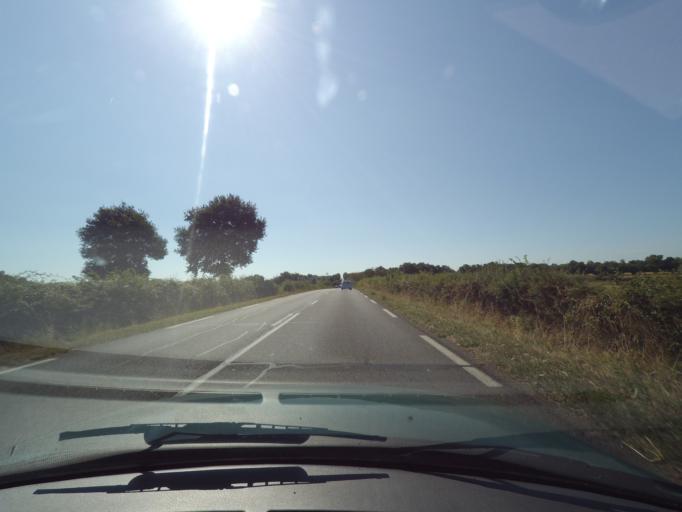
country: FR
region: Limousin
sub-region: Departement de la Haute-Vienne
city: Peyrat-de-Bellac
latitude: 46.1398
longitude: 0.9788
